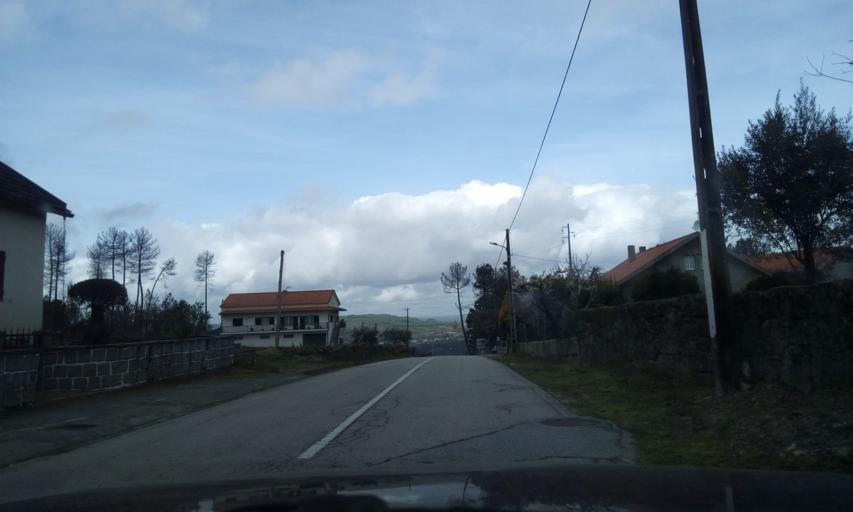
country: PT
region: Guarda
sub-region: Fornos de Algodres
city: Fornos de Algodres
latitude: 40.6623
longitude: -7.5999
